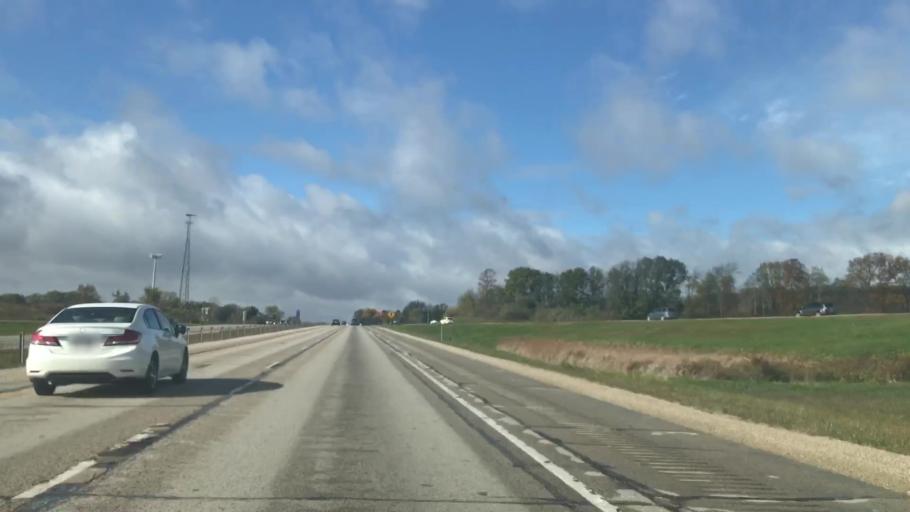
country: US
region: Wisconsin
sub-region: Washington County
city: Richfield
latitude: 43.2828
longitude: -88.1949
